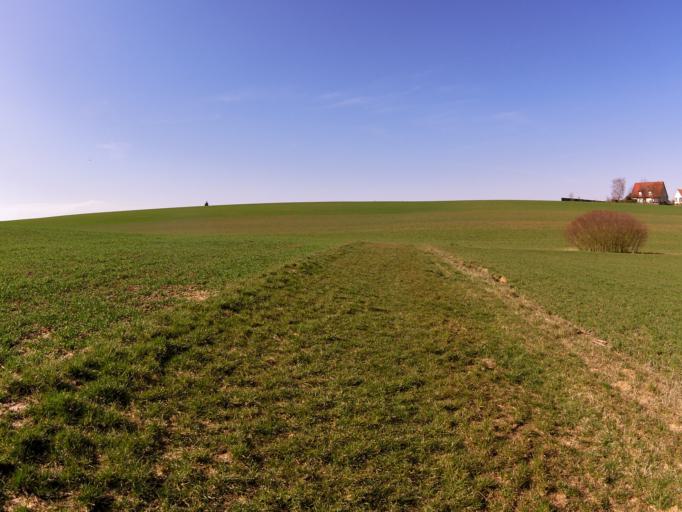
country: DE
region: Bavaria
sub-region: Regierungsbezirk Unterfranken
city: Prosselsheim
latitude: 49.8594
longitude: 10.1208
